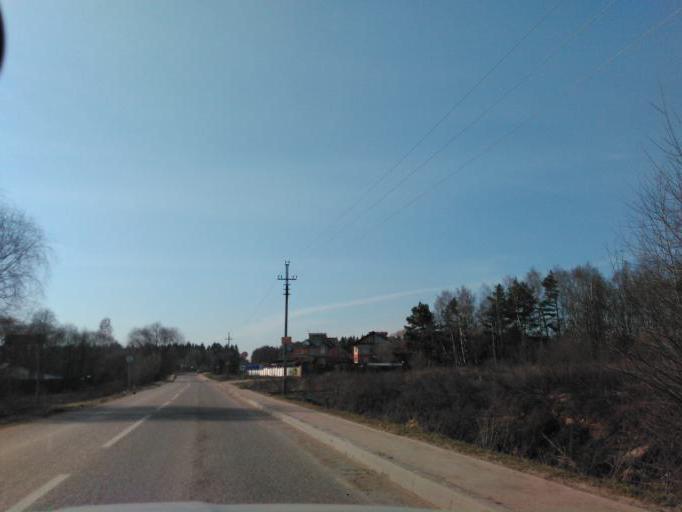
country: RU
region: Moskovskaya
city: Skhodnya
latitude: 55.8966
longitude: 37.2702
